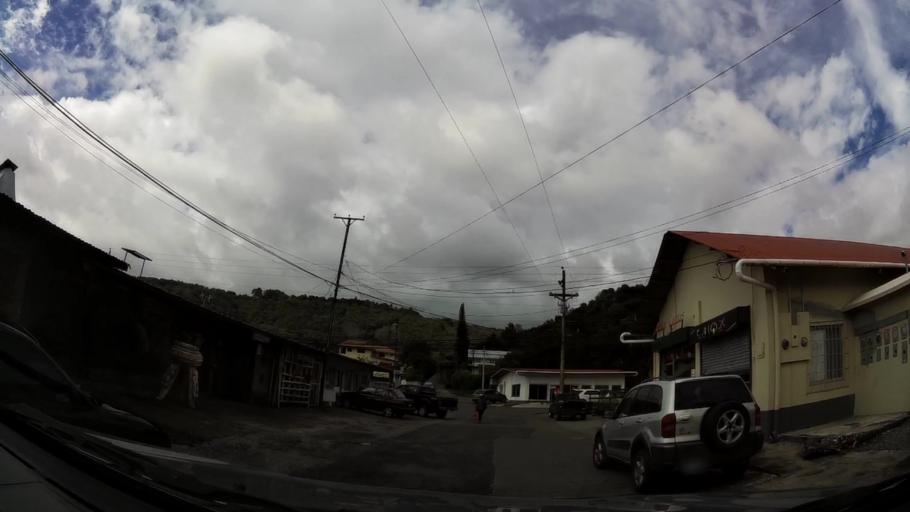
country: PA
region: Chiriqui
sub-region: Distrito Boquete
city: Boquete
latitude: 8.7777
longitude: -82.4331
